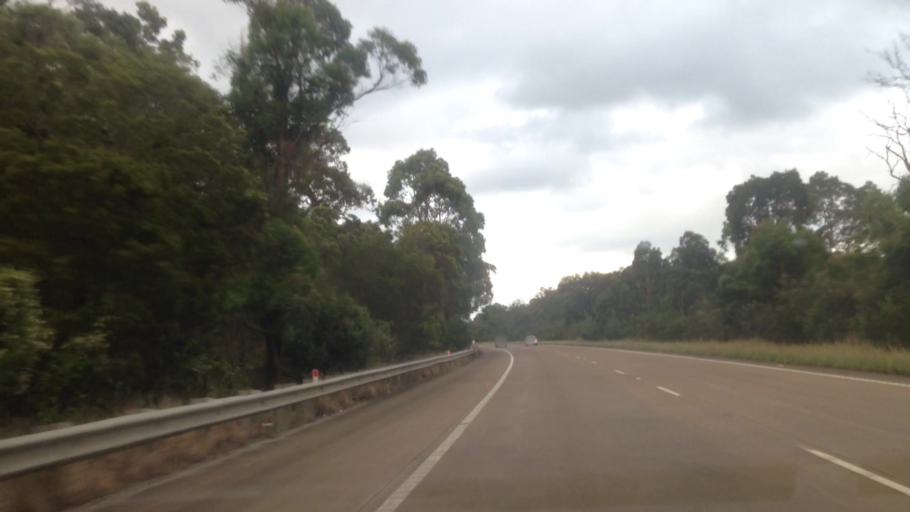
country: AU
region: New South Wales
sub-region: Lake Macquarie Shire
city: Dora Creek
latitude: -33.1475
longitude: 151.4744
